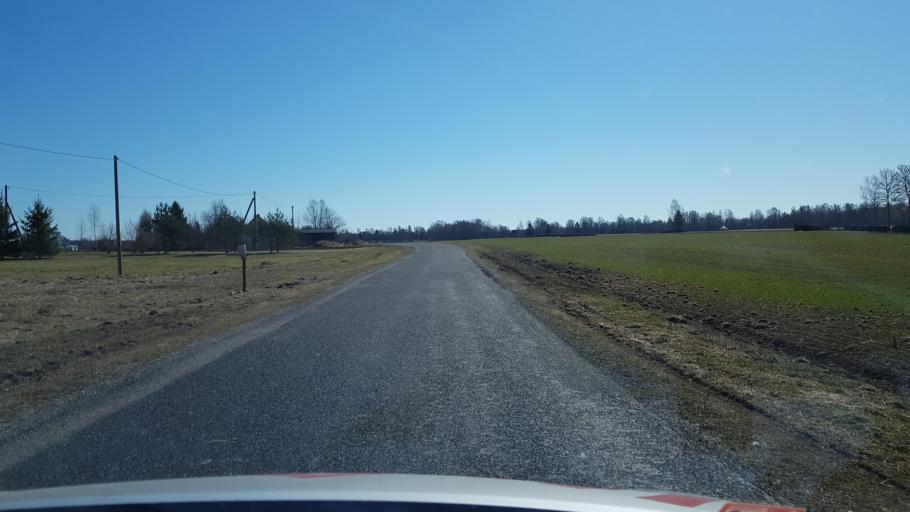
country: EE
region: Laeaene-Virumaa
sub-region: Kadrina vald
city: Kadrina
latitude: 59.4429
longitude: 26.1167
